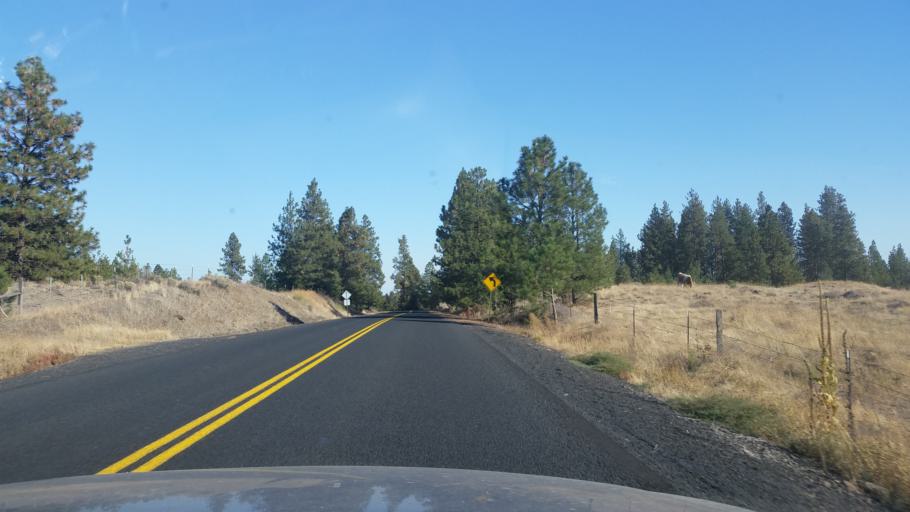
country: US
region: Washington
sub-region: Spokane County
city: Cheney
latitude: 47.3594
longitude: -117.6971
